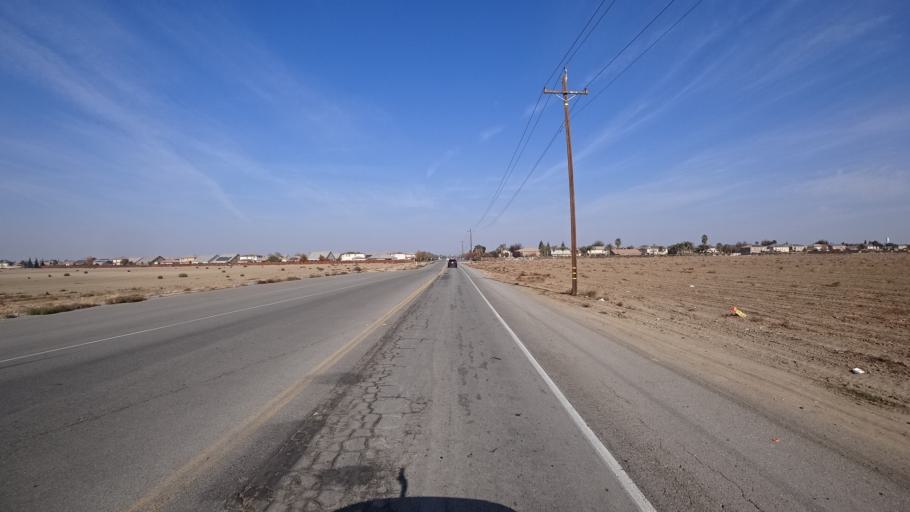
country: US
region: California
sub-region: Kern County
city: Greenacres
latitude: 35.2979
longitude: -119.1099
